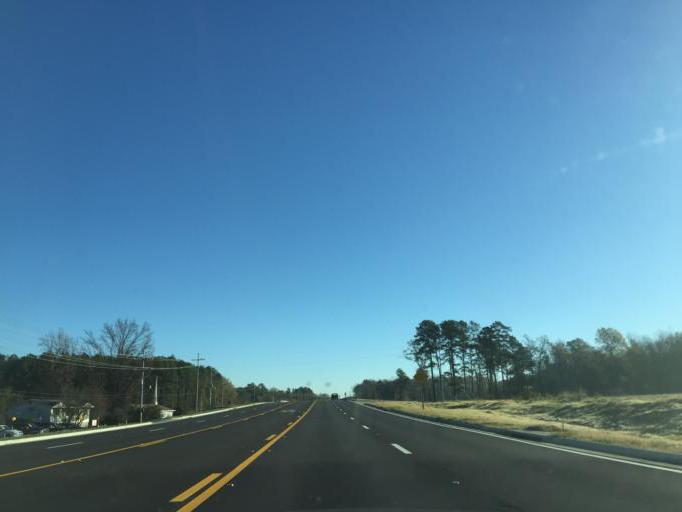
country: US
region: Mississippi
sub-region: Rankin County
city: Flowood
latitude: 32.3200
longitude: -90.1252
